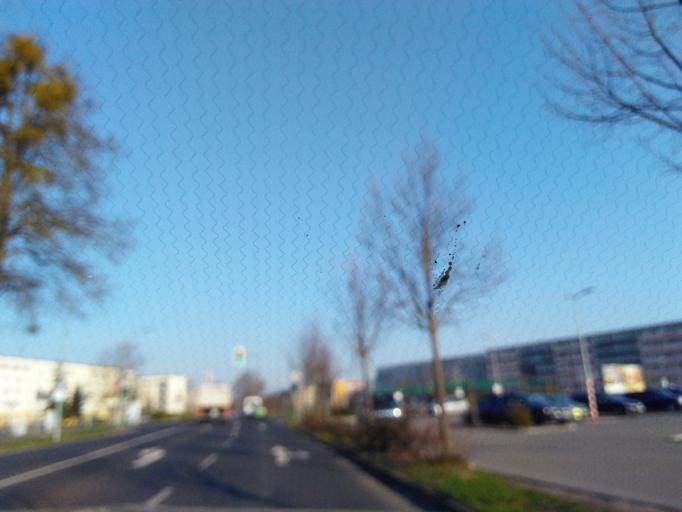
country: DE
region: Brandenburg
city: Strausberg
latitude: 52.5732
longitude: 13.8963
